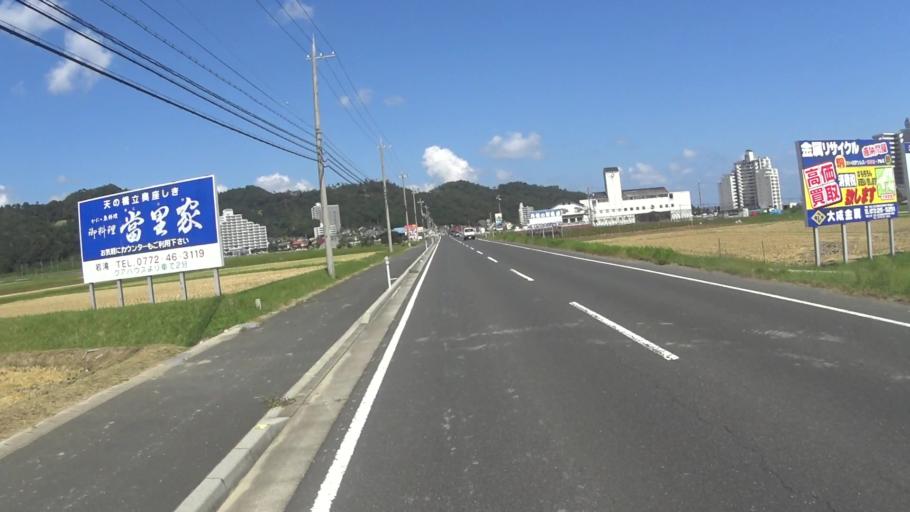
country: JP
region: Kyoto
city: Miyazu
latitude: 35.6112
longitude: 135.2282
